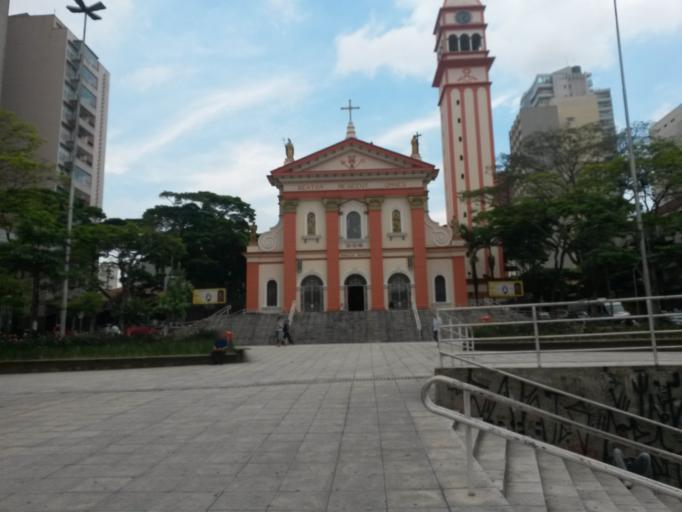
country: BR
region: Sao Paulo
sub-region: Sao Bernardo Do Campo
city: Sao Bernardo do Campo
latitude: -23.7080
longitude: -46.5506
